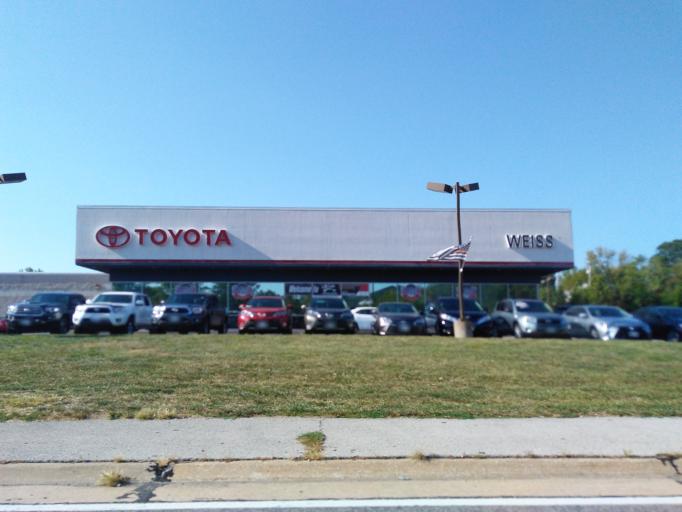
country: US
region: Missouri
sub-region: Saint Louis County
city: Concord
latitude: 38.5212
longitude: -90.3587
